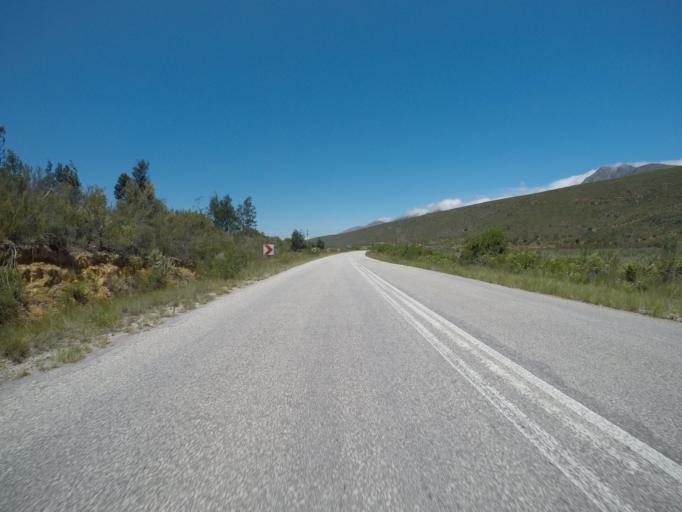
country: ZA
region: Eastern Cape
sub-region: Cacadu District Municipality
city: Kareedouw
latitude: -33.8752
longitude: 24.0503
